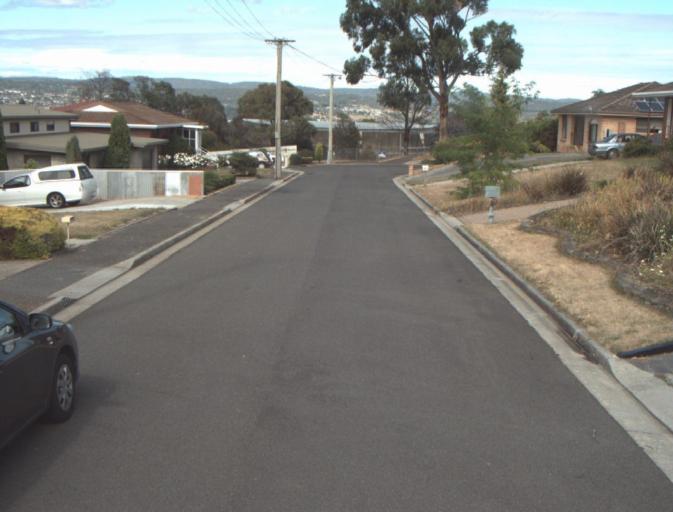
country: AU
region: Tasmania
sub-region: Launceston
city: Mayfield
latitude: -41.3811
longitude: 147.1275
